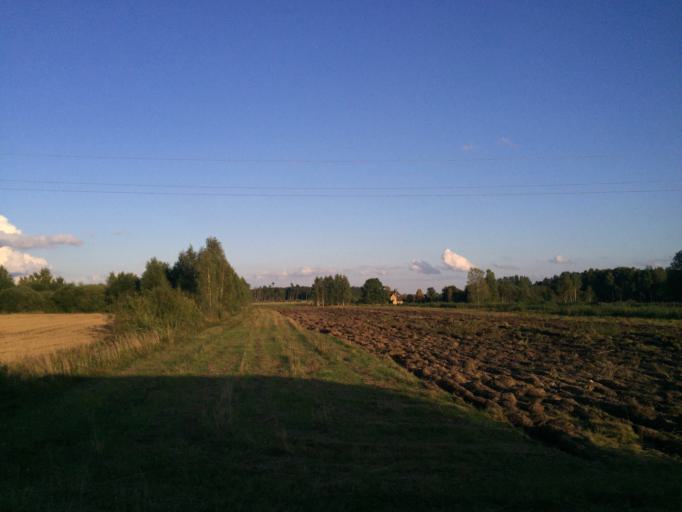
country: LV
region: Tukuma Rajons
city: Tukums
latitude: 56.8877
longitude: 23.2245
